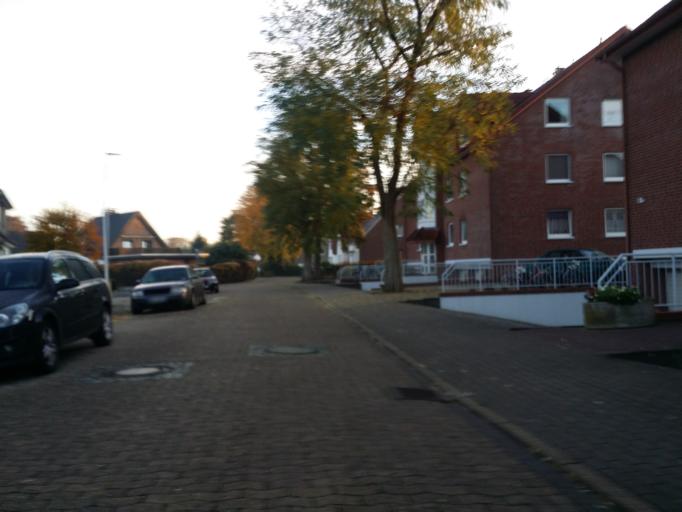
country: DE
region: Lower Saxony
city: Delmenhorst
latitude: 53.0293
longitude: 8.6461
